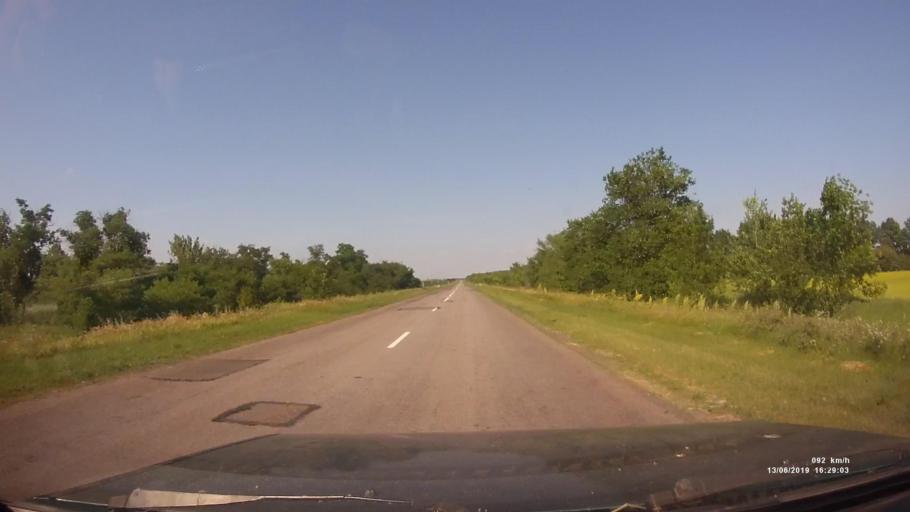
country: RU
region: Rostov
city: Kazanskaya
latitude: 49.8268
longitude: 41.2109
